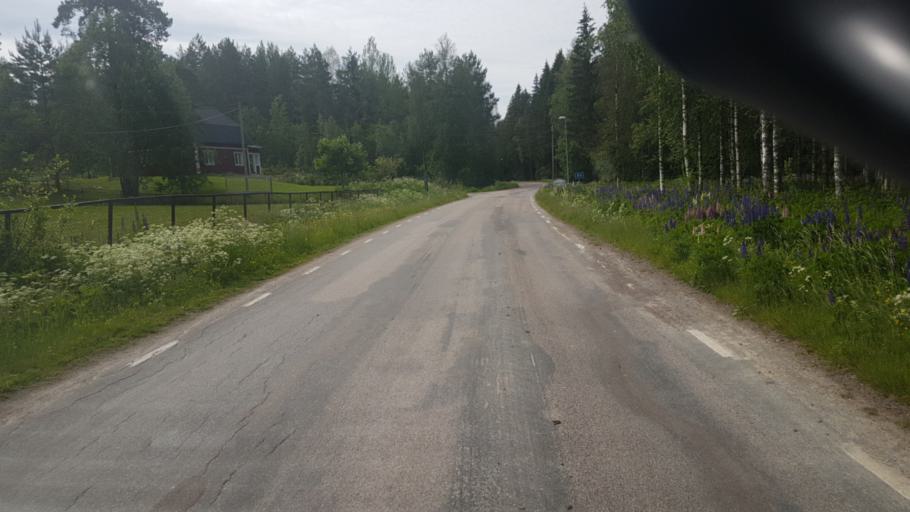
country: SE
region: Vaermland
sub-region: Eda Kommun
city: Charlottenberg
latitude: 59.8560
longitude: 12.3428
